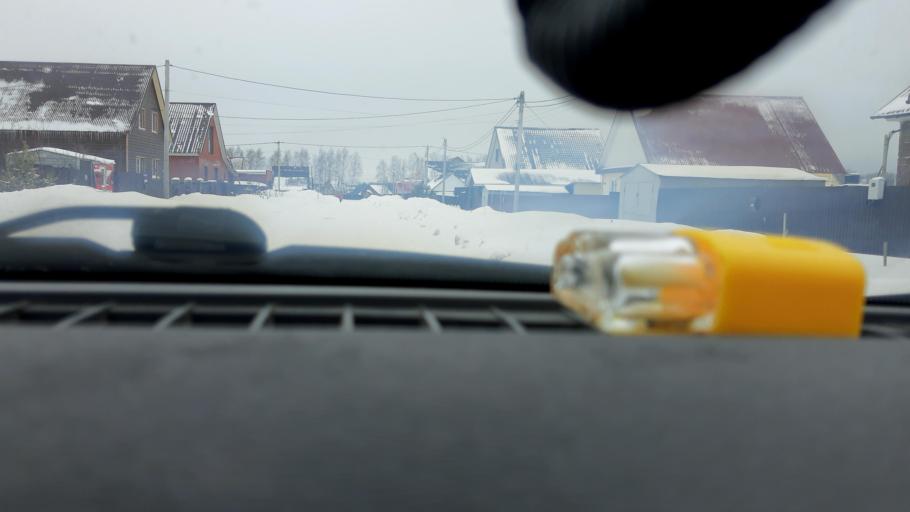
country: RU
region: Bashkortostan
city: Iglino
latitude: 54.8325
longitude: 56.4452
